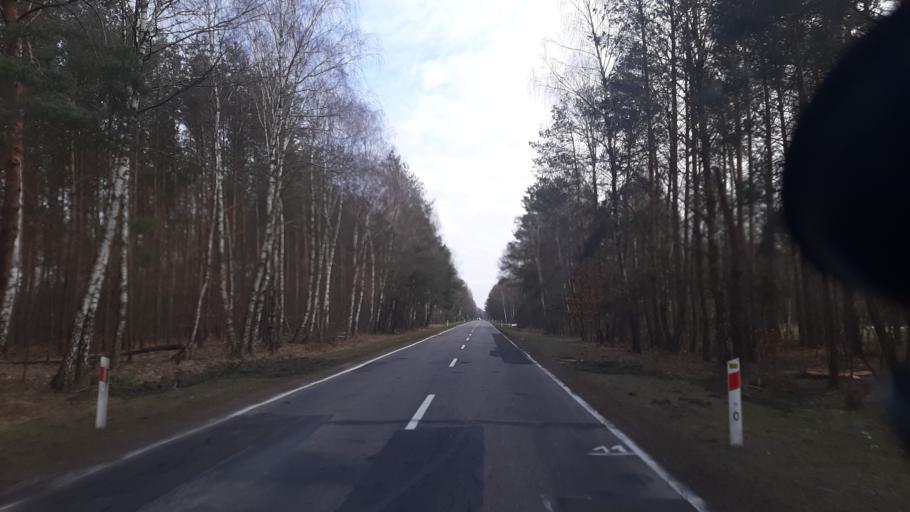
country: PL
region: Lublin Voivodeship
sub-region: Powiat lubartowski
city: Ostrow Lubelski
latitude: 51.4907
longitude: 22.8055
